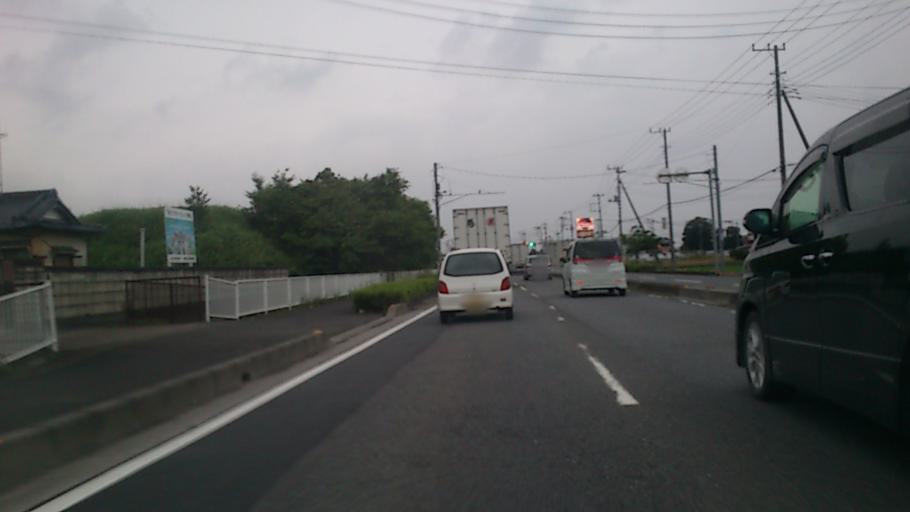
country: JP
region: Saitama
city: Hanyu
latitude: 36.1690
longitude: 139.5785
